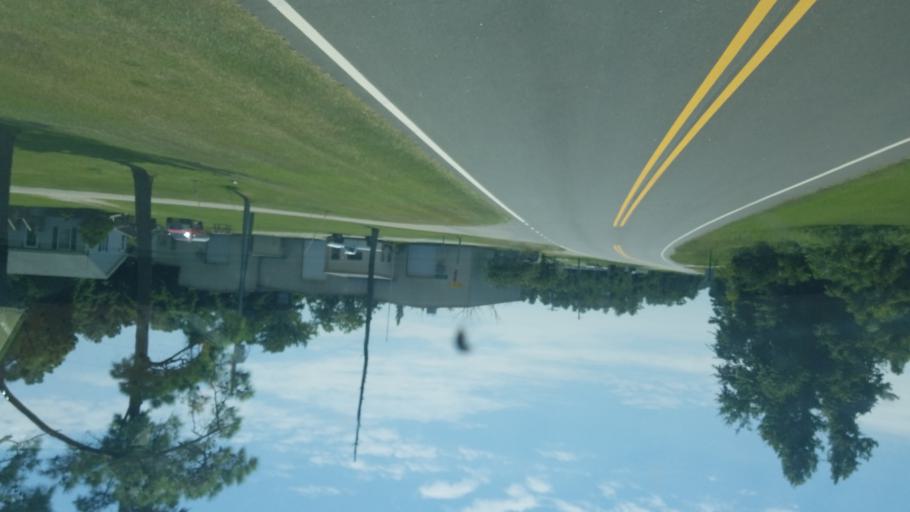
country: US
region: North Carolina
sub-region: Dare County
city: Manteo
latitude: 35.9058
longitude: -75.7743
